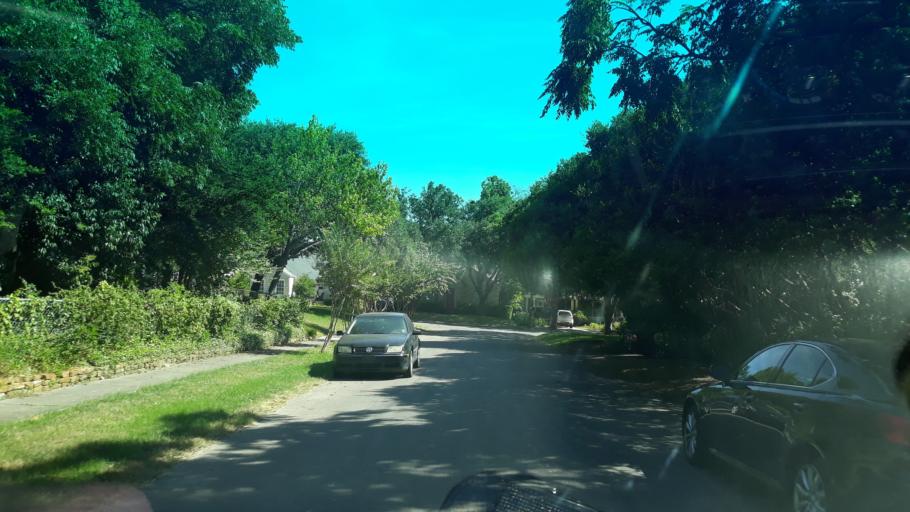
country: US
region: Texas
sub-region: Dallas County
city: Highland Park
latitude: 32.8156
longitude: -96.7589
